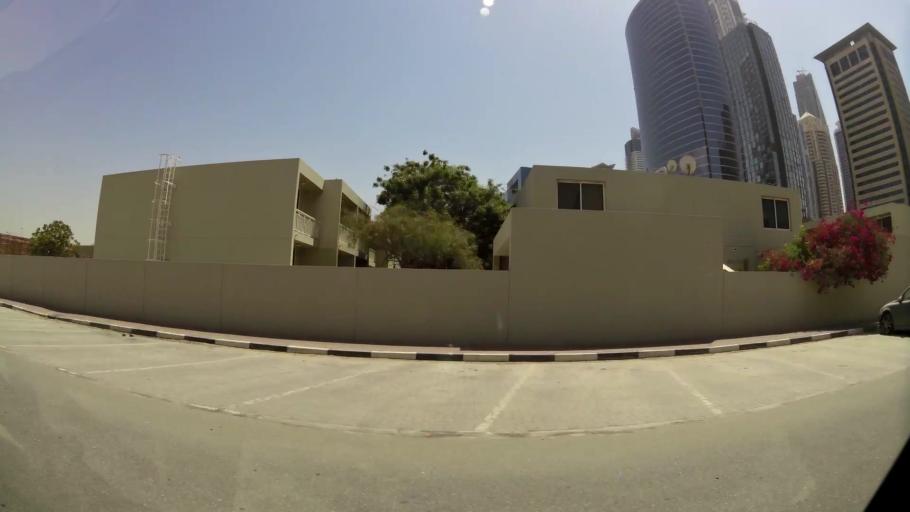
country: AE
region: Dubai
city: Dubai
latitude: 25.0899
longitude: 55.1550
